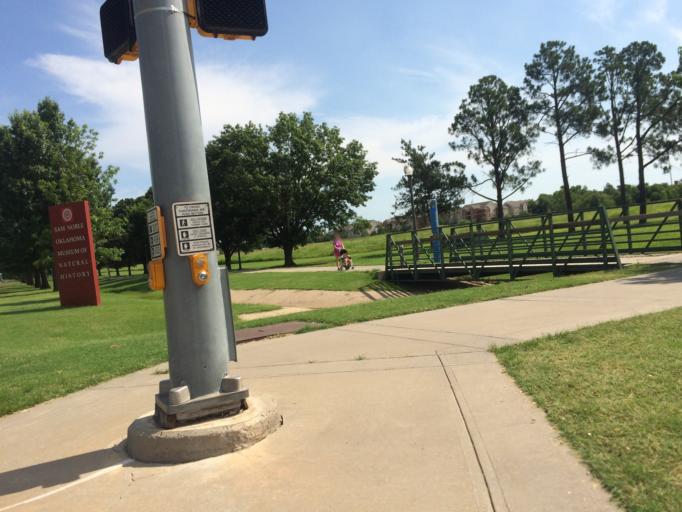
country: US
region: Oklahoma
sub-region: Cleveland County
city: Norman
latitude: 35.1896
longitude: -97.4499
